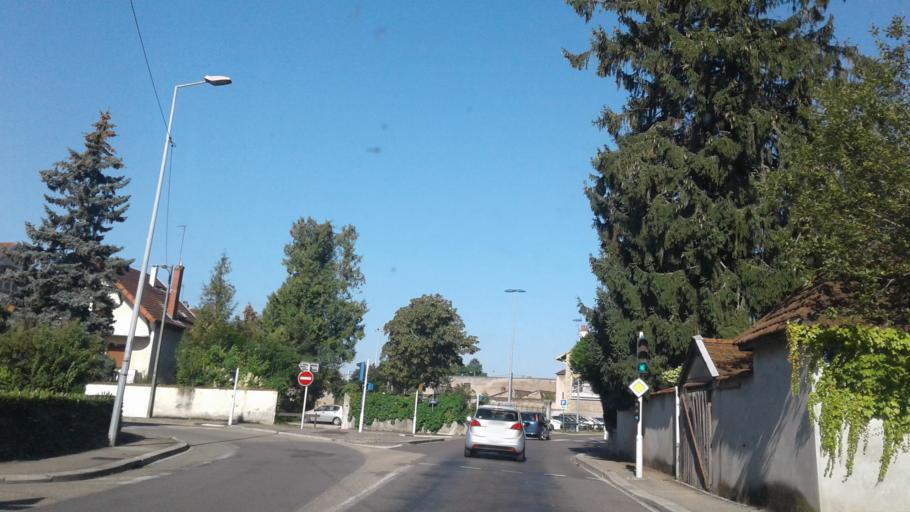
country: FR
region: Rhone-Alpes
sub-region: Departement de l'Ain
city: Bourg-en-Bresse
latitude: 46.1958
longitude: 5.2198
